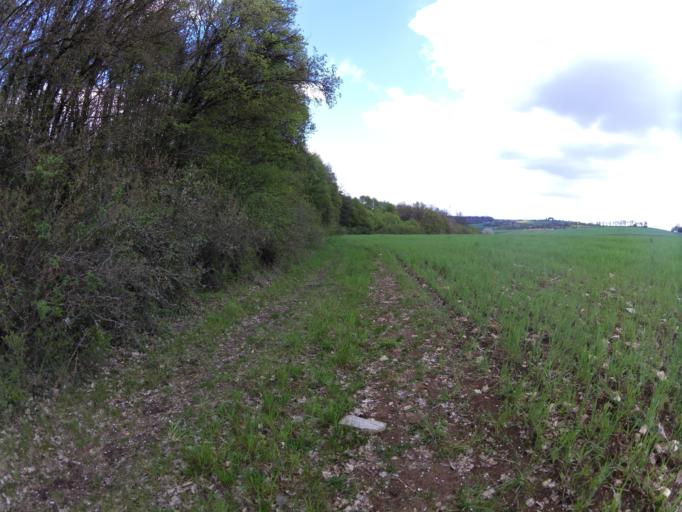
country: DE
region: Bavaria
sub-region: Regierungsbezirk Unterfranken
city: Hettstadt
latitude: 49.7932
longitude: 9.7898
